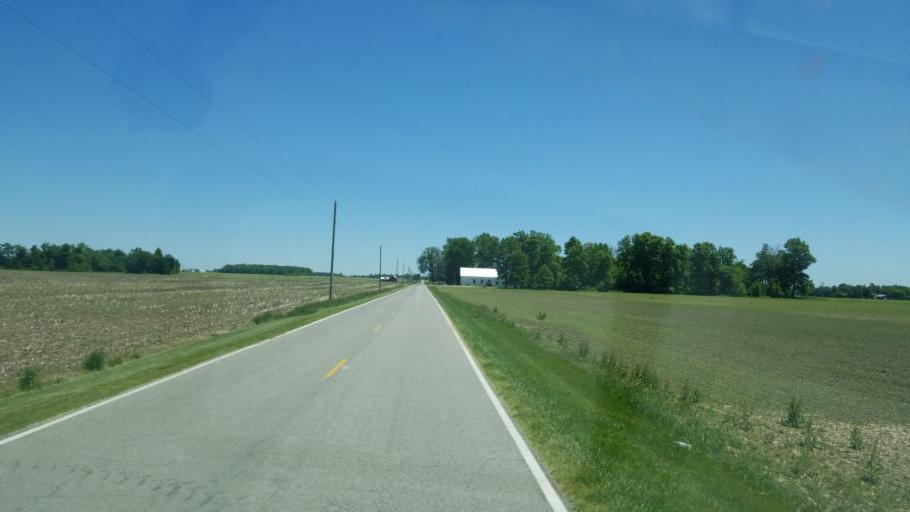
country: US
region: Indiana
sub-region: Randolph County
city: Union City
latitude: 40.2815
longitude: -84.7555
